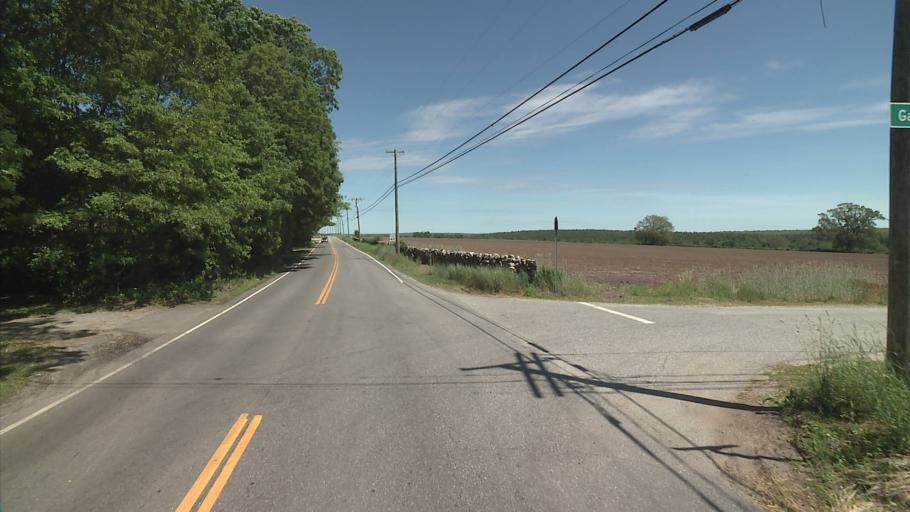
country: US
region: Rhode Island
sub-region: Washington County
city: Hopkinton
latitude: 41.5378
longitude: -71.8393
